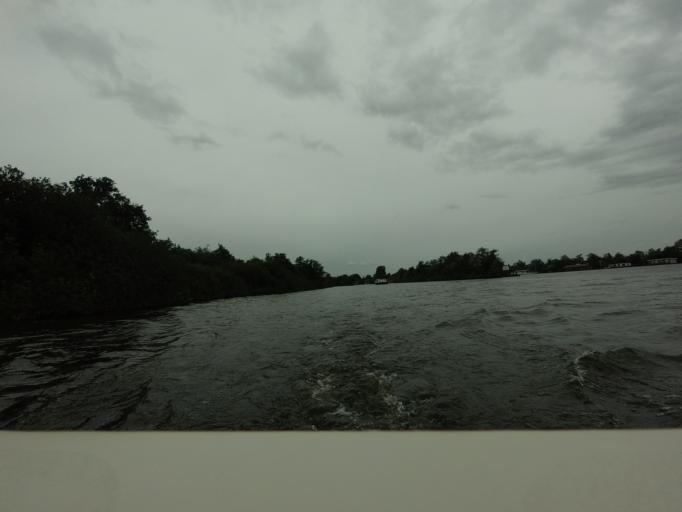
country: NL
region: Friesland
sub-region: Gemeente Tytsjerksteradiel
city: Garyp
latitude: 53.1197
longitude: 5.9440
